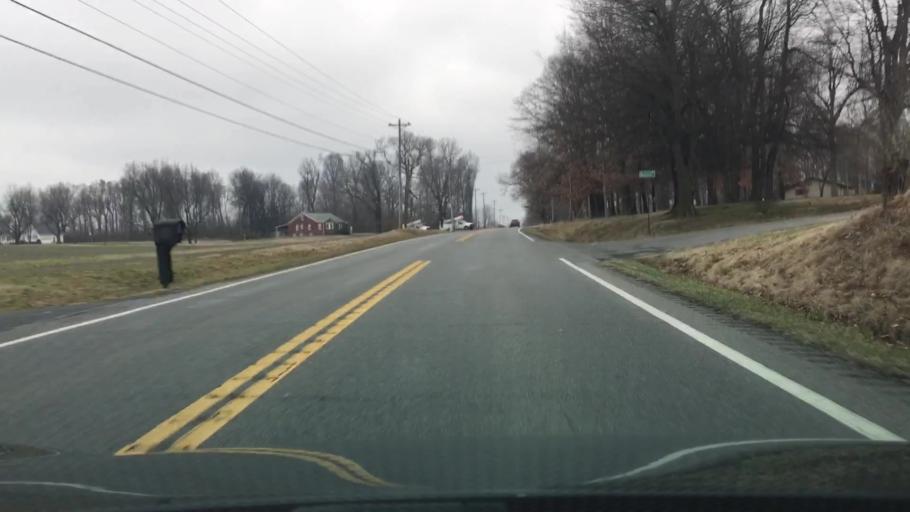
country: US
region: Kentucky
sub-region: Marshall County
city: Calvert City
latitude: 36.9493
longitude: -88.3677
